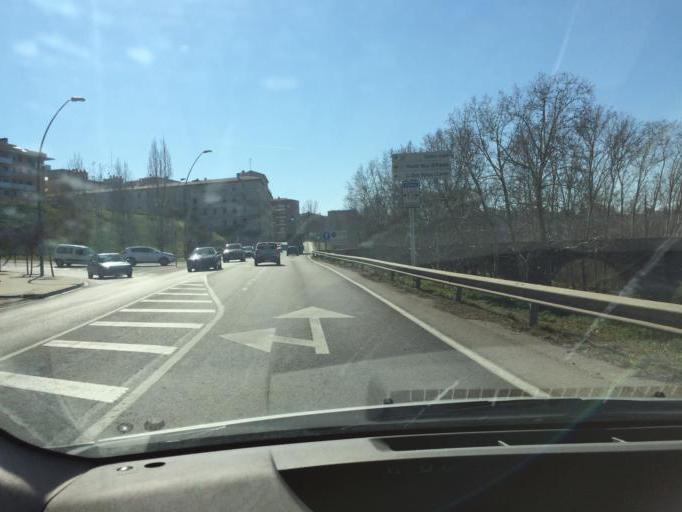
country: ES
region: Catalonia
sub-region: Provincia de Barcelona
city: Manresa
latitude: 41.7288
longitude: 1.8146
